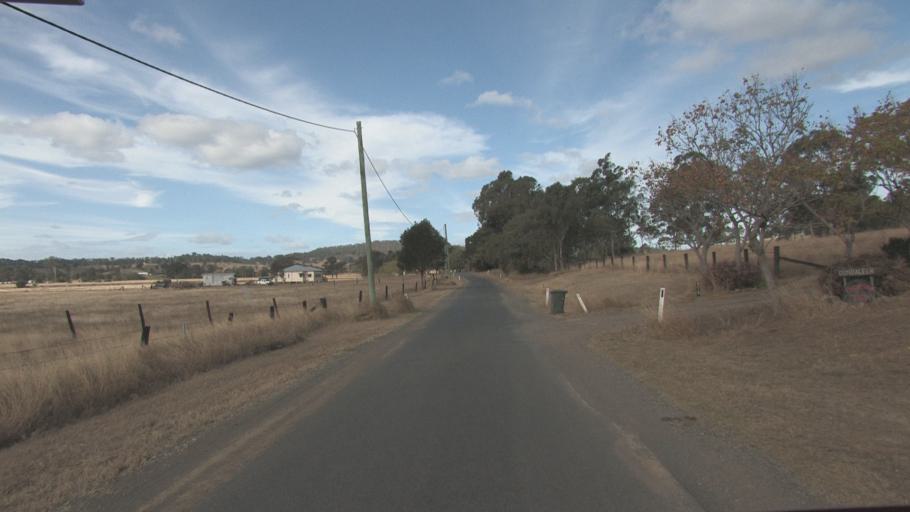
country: AU
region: Queensland
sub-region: Logan
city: Cedar Vale
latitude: -27.9190
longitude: 153.0035
